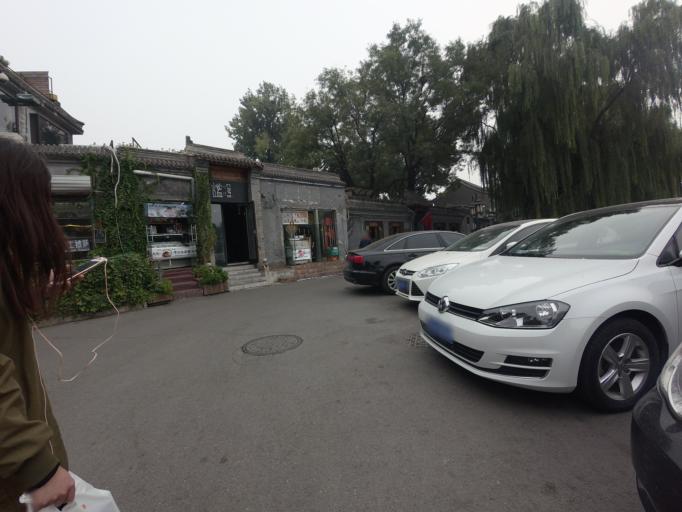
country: CN
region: Beijing
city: Jingshan
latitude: 39.9348
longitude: 116.3890
